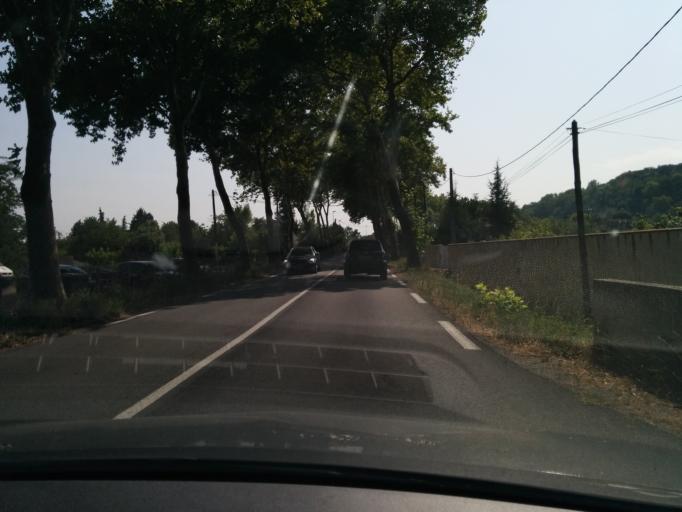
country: FR
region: Midi-Pyrenees
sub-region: Departement du Tarn
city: Albi
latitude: 43.9501
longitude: 2.1233
